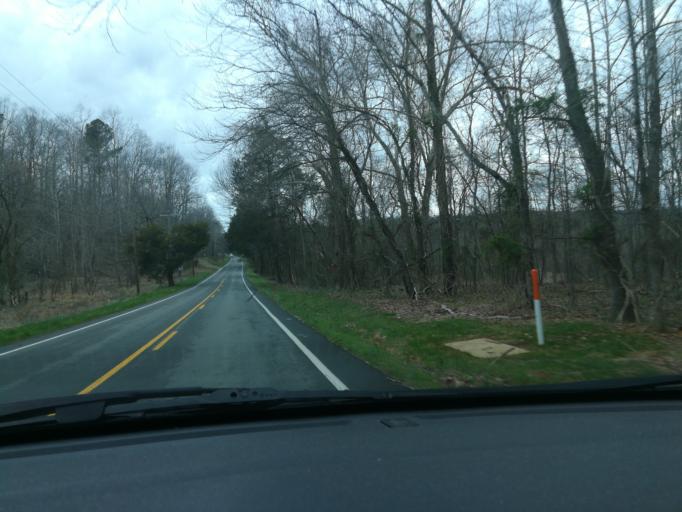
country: US
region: North Carolina
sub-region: Orange County
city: Hillsborough
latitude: 36.0338
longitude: -79.0437
